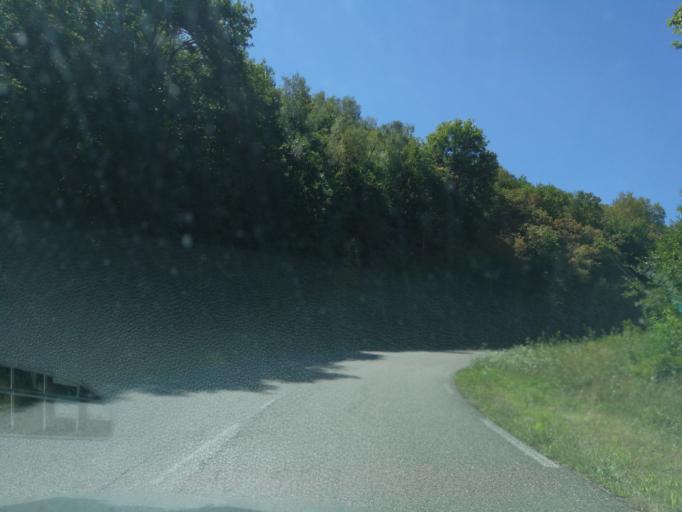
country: FR
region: Limousin
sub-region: Departement de la Correze
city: Argentat
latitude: 45.0621
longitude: 1.9469
